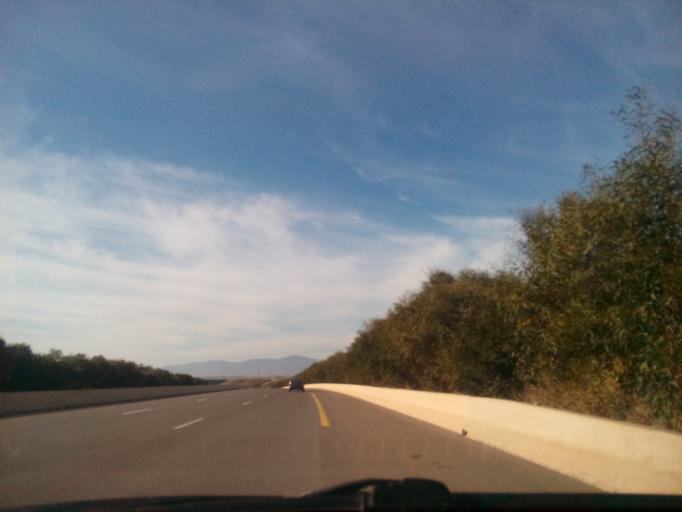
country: DZ
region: Tlemcen
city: Beni Mester
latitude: 34.9204
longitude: -1.4401
